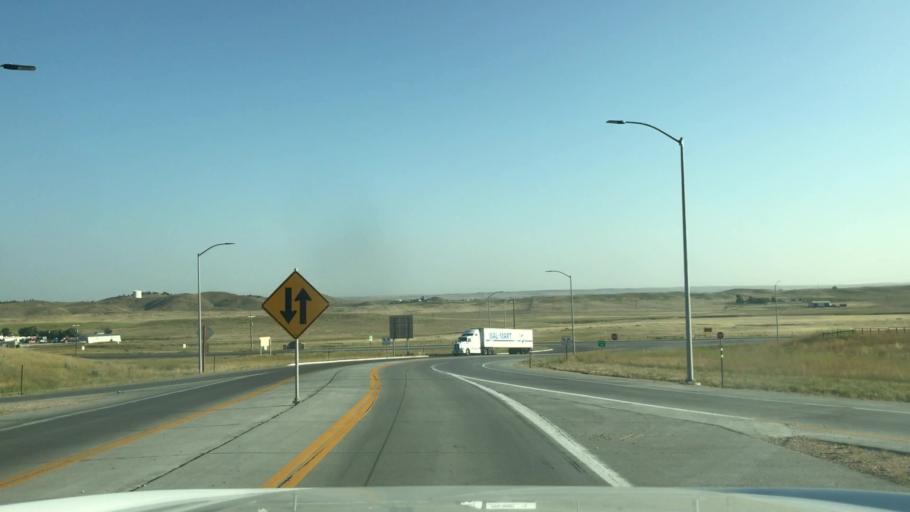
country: US
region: Wyoming
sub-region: Converse County
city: Douglas
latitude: 42.7338
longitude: -105.3418
